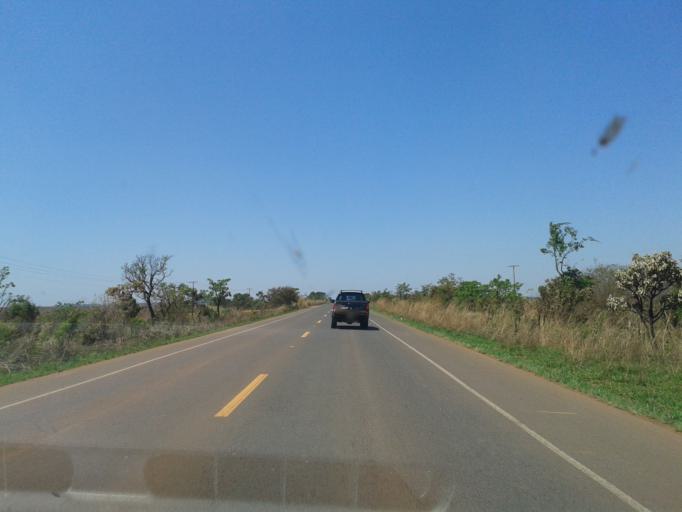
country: BR
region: Minas Gerais
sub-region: Araxa
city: Araxa
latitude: -19.3419
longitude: -47.3719
